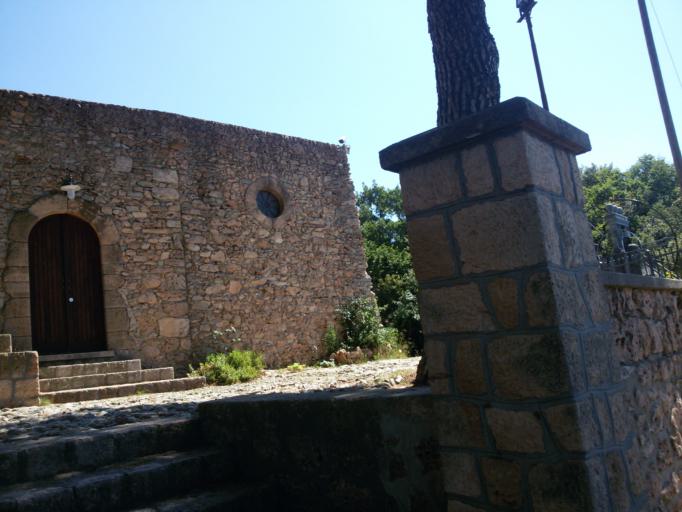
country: IT
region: Liguria
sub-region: Provincia di Savona
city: Borgio
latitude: 44.1684
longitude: 8.3155
